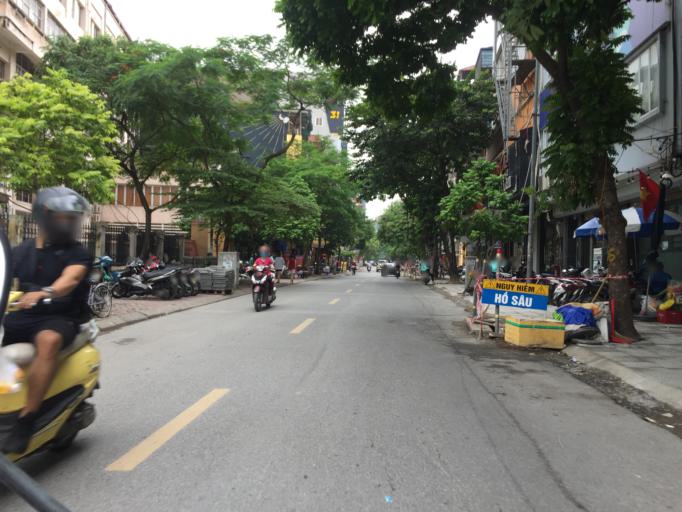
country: VN
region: Ha Noi
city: Cau Giay
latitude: 21.0230
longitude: 105.8086
